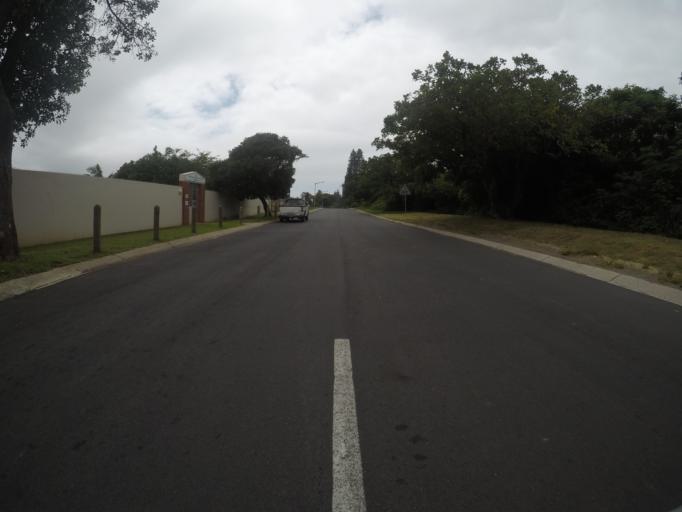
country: ZA
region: Eastern Cape
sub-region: Buffalo City Metropolitan Municipality
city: East London
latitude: -32.9929
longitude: 27.9308
